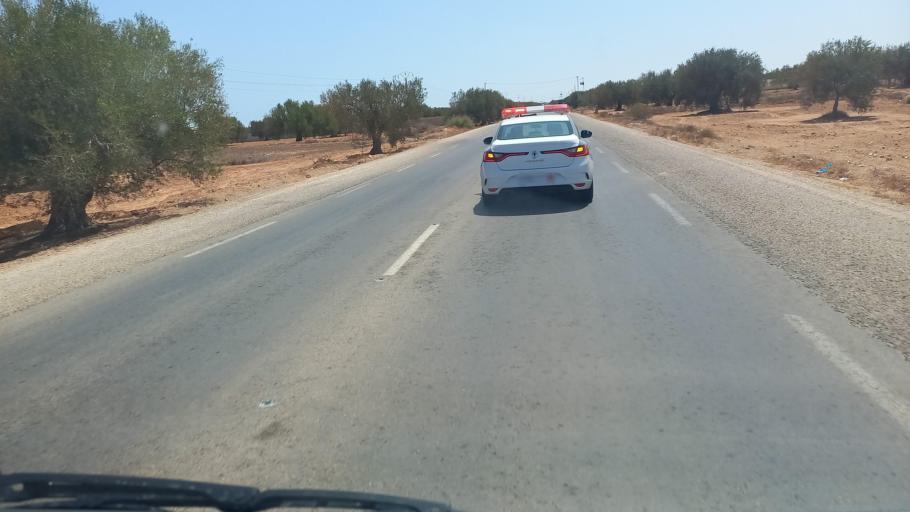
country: TN
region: Madanin
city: Zarzis
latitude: 33.5661
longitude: 11.0483
